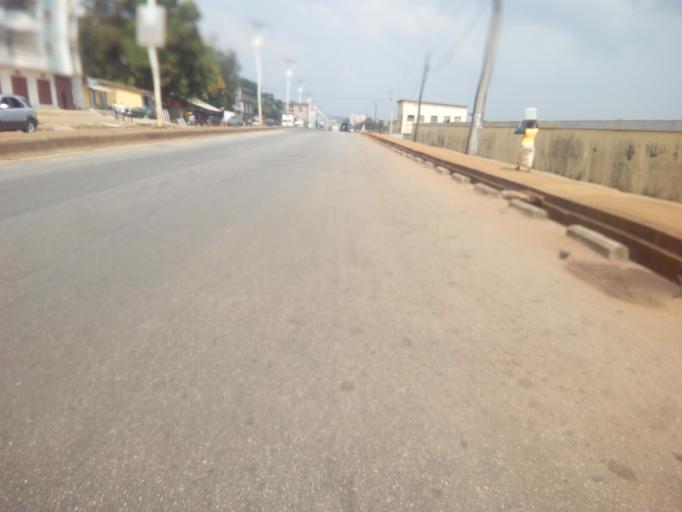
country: GN
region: Conakry
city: Conakry
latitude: 9.6273
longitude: -13.5771
